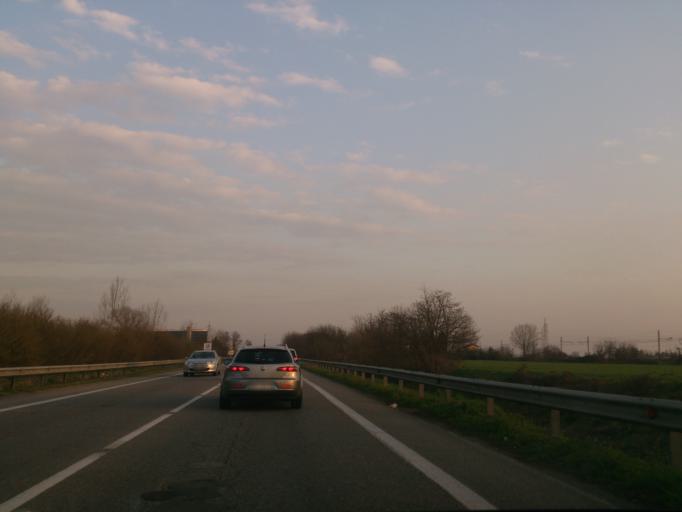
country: IT
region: Lombardy
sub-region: Citta metropolitana di Milano
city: San Giuliano Milanese
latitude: 45.3879
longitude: 9.2924
